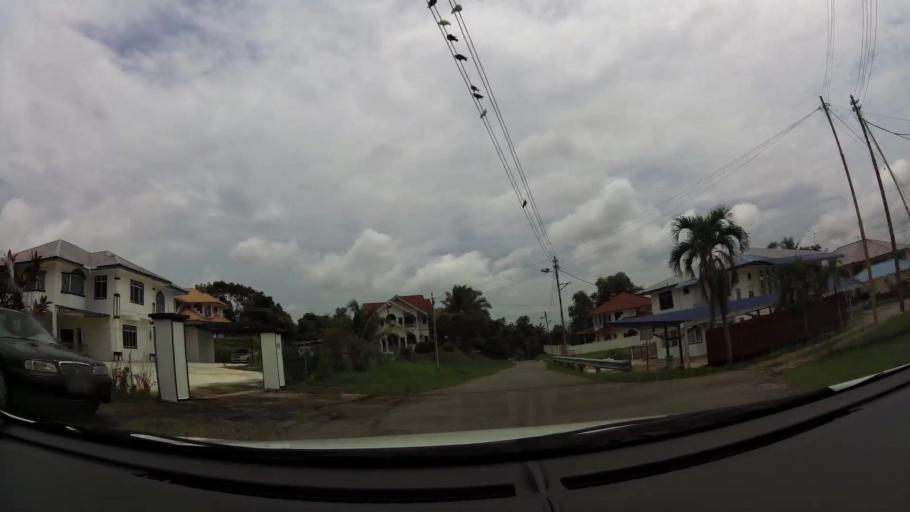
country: BN
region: Brunei and Muara
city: Bandar Seri Begawan
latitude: 4.8930
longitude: 114.9249
